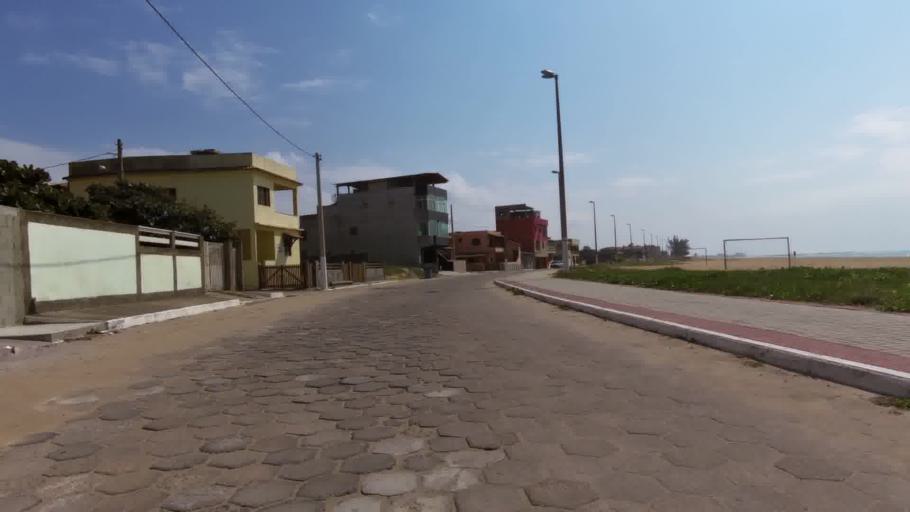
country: BR
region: Espirito Santo
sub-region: Marataizes
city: Marataizes
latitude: -21.0322
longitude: -40.8128
